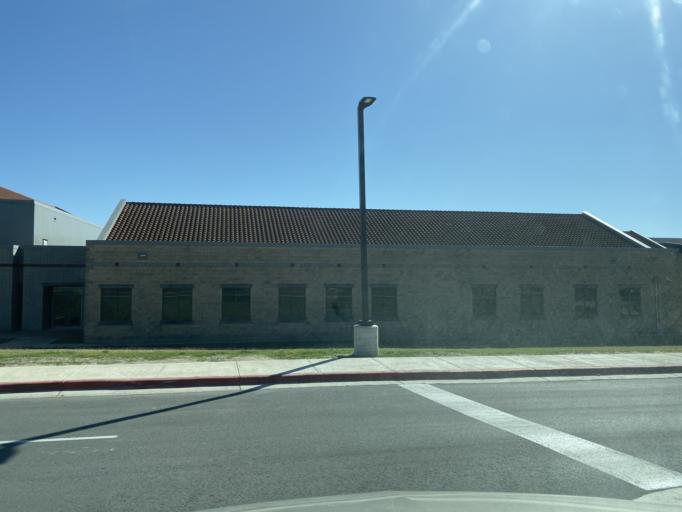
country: US
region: Texas
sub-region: Travis County
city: The Hills
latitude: 30.3277
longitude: -97.9707
